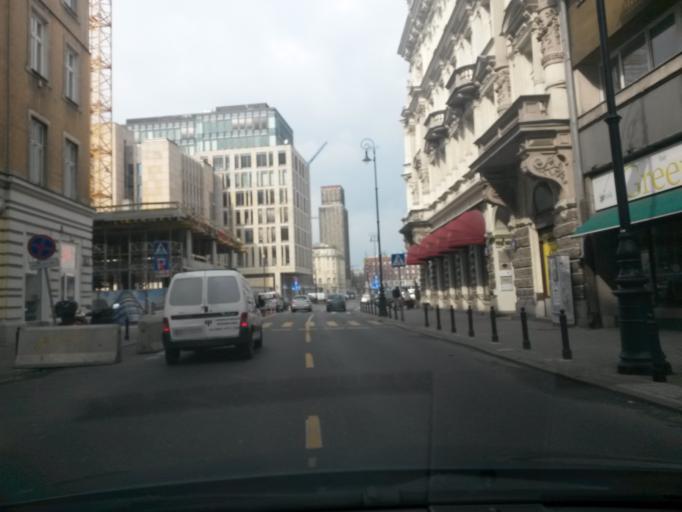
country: PL
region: Masovian Voivodeship
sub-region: Warszawa
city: Srodmiescie
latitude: 52.2329
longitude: 21.0149
